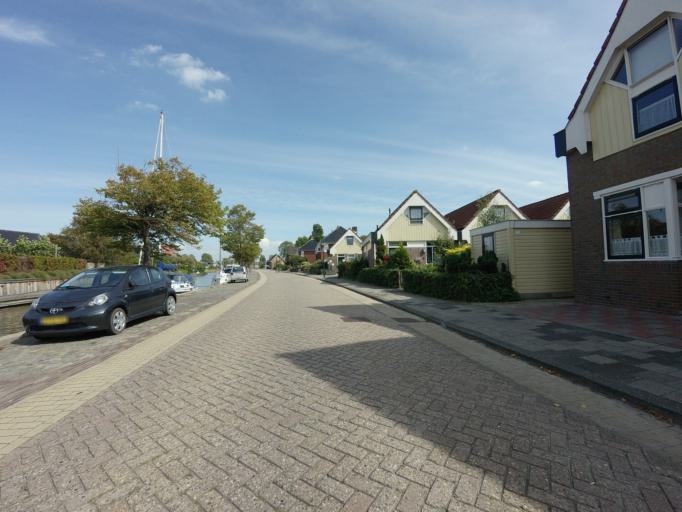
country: NL
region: Friesland
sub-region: Gemeente Harlingen
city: Harlingen
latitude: 53.1740
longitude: 5.4263
